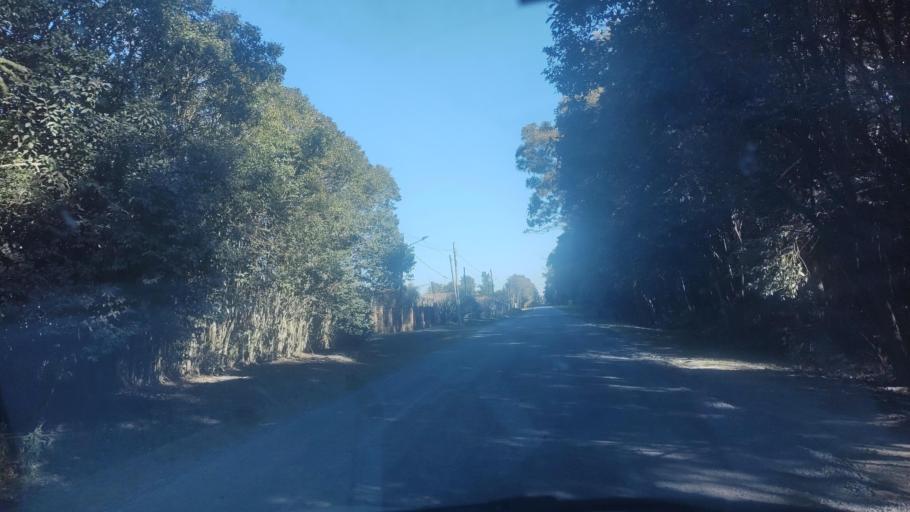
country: AR
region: Buenos Aires
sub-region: Partido de La Plata
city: La Plata
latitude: -34.8490
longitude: -58.1007
